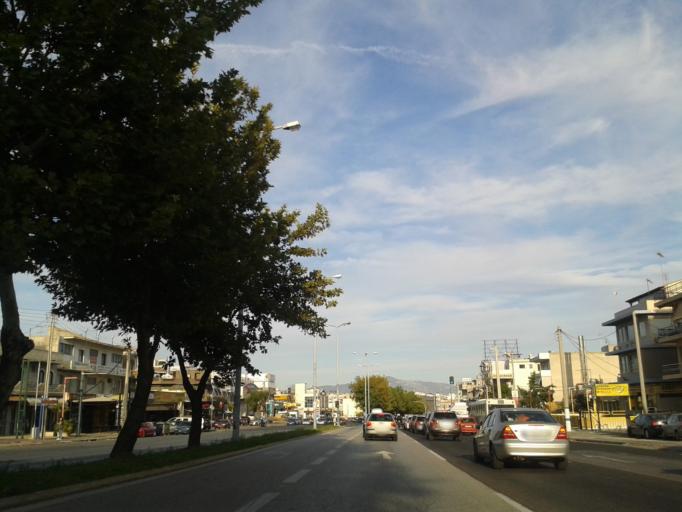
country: GR
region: Attica
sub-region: Nomarchia Athinas
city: Chaidari
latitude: 38.0115
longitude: 23.6529
